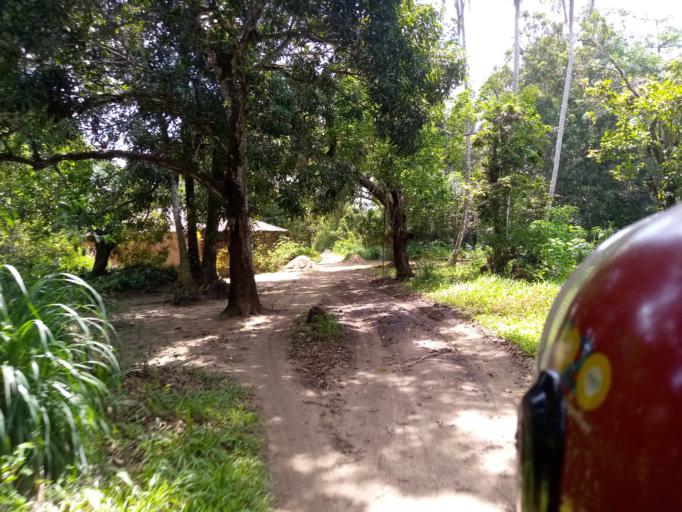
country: SL
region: Western Area
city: Waterloo
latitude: 8.3703
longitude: -13.0012
